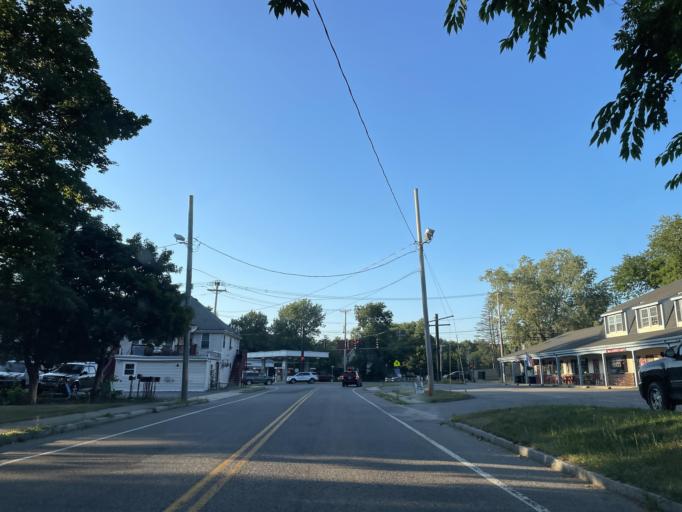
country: US
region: Massachusetts
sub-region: Plymouth County
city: Hanson
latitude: 42.0428
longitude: -70.8422
